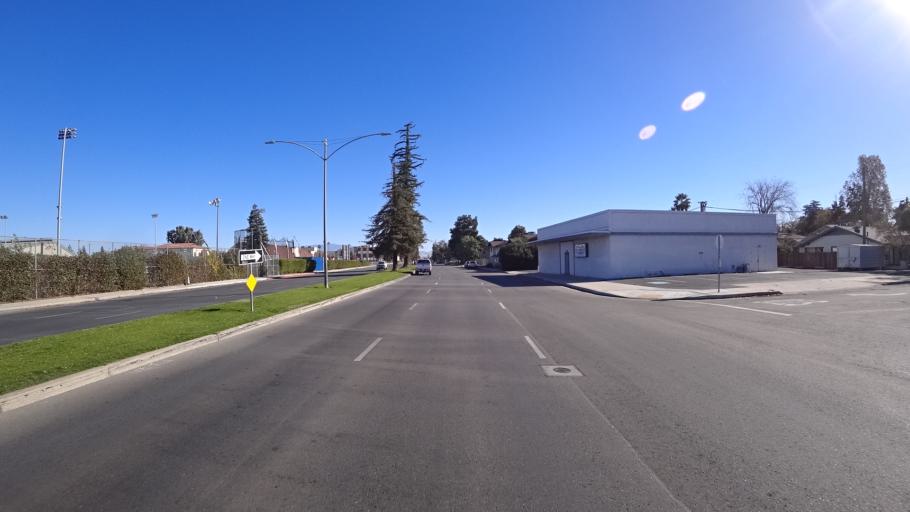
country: US
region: California
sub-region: Kern County
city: Bakersfield
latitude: 35.3685
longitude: -119.0275
